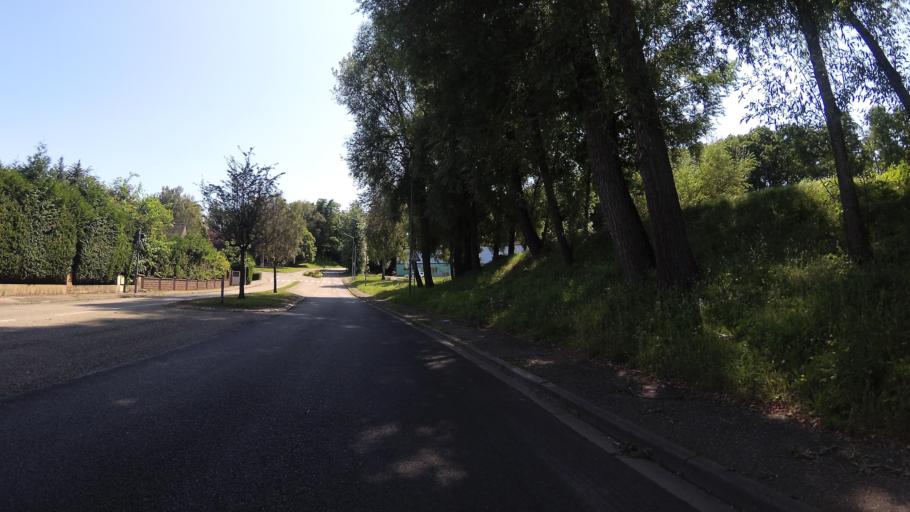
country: FR
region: Lorraine
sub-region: Departement de la Moselle
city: Stiring-Wendel
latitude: 49.2062
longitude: 6.9359
